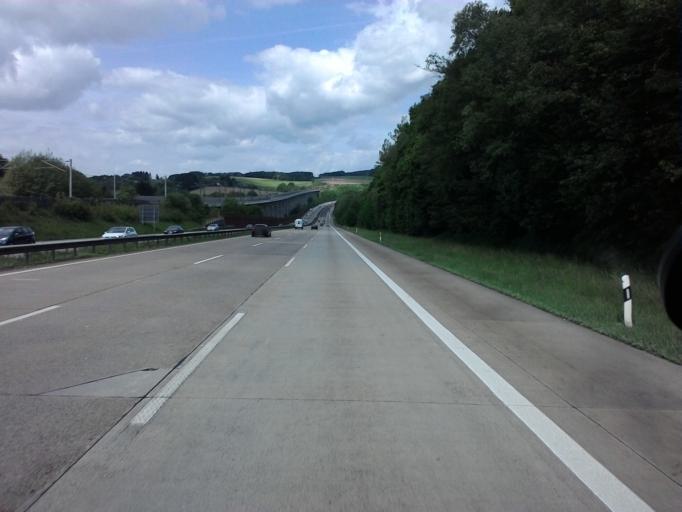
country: DE
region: Rheinland-Pfalz
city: Rossbach
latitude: 50.6208
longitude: 7.4022
